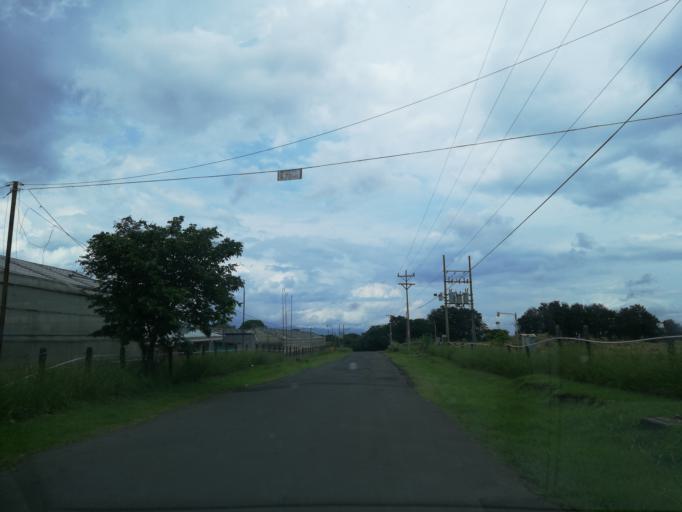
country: CR
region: Alajuela
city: Alajuela
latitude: 10.0333
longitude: -84.1914
